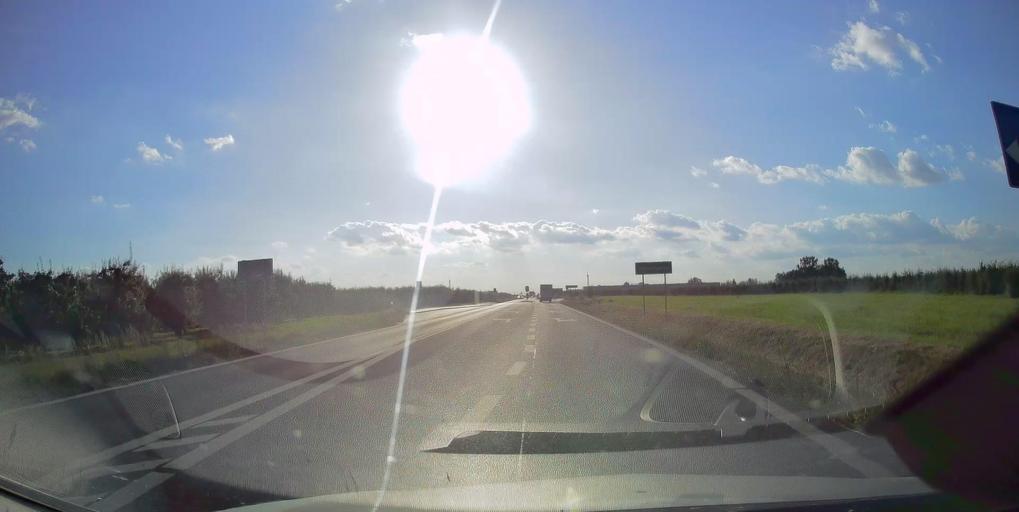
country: PL
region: Lodz Voivodeship
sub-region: Powiat rawski
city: Sadkowice
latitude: 51.8059
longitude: 20.5782
